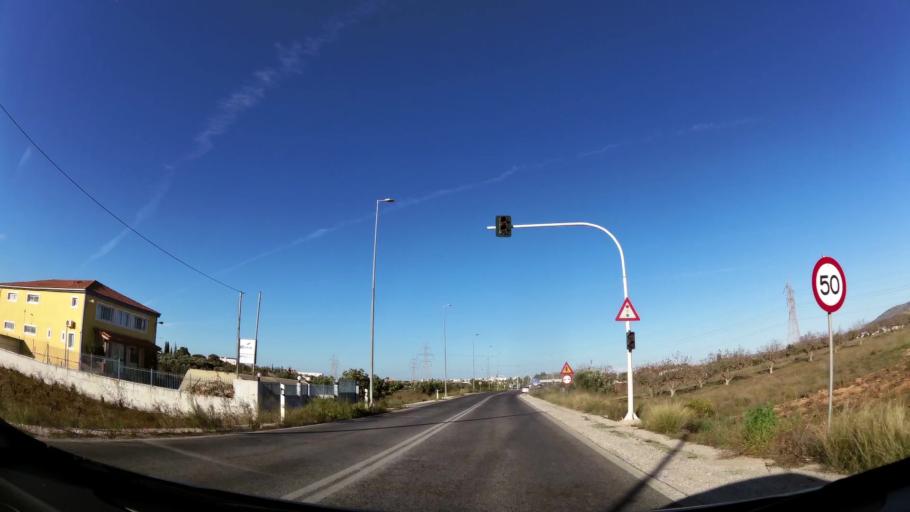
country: GR
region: Attica
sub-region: Nomarchia Anatolikis Attikis
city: Kalyvia Thorikou
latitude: 37.8620
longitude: 23.9235
